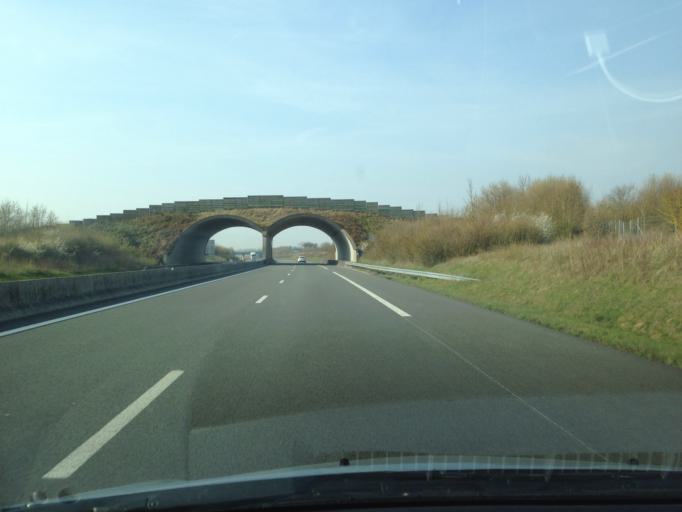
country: FR
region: Picardie
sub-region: Departement de la Somme
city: Nouvion
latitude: 50.2578
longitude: 1.7479
